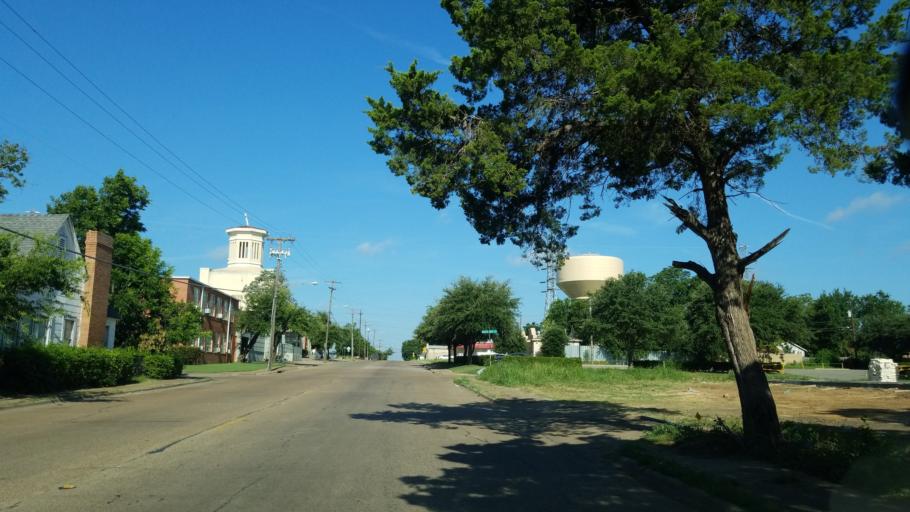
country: US
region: Texas
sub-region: Dallas County
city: Dallas
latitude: 32.7132
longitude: -96.8092
